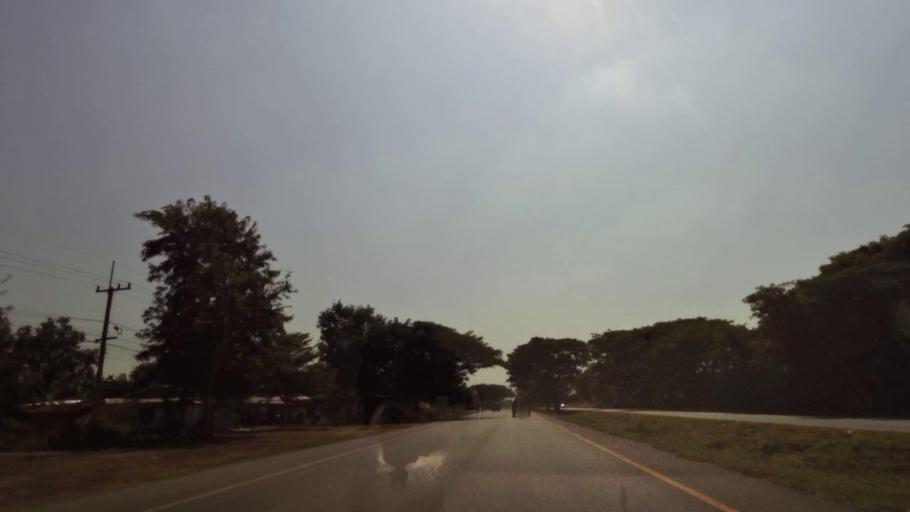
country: TH
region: Phichit
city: Bueng Na Rang
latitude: 16.3394
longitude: 100.1283
